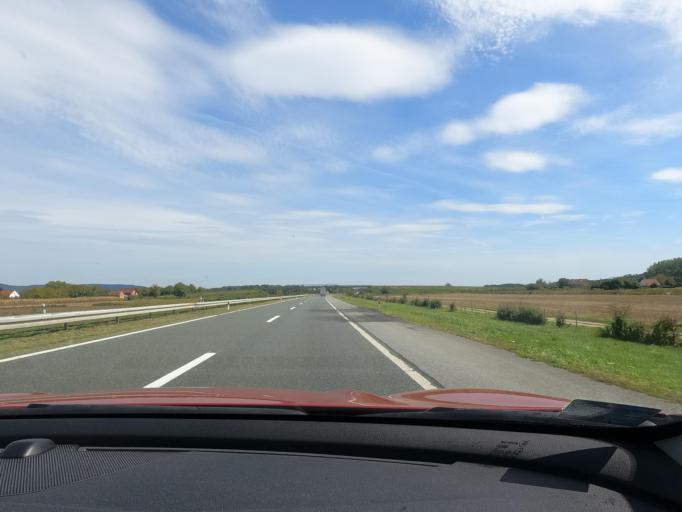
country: HR
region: Brodsko-Posavska
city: Resetari
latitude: 45.2305
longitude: 17.4558
